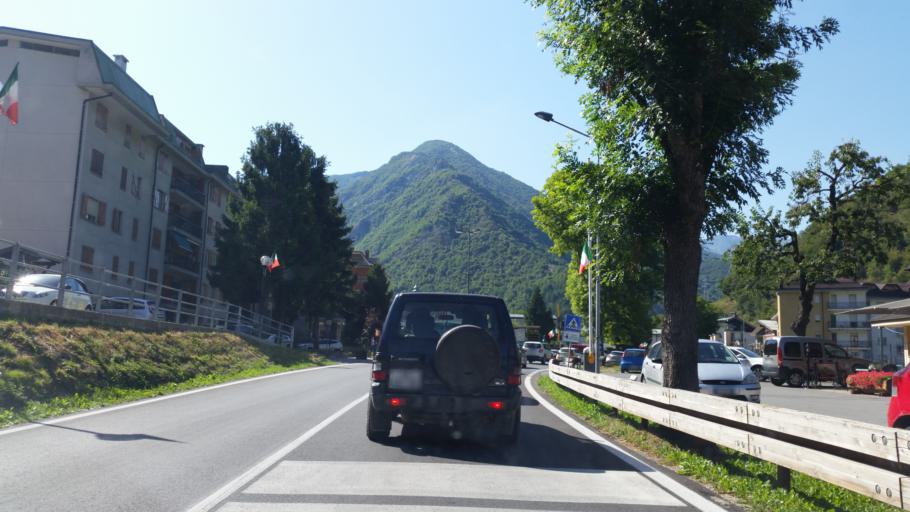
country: IT
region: Piedmont
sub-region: Provincia di Cuneo
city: Vernante
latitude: 44.2488
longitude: 7.5321
